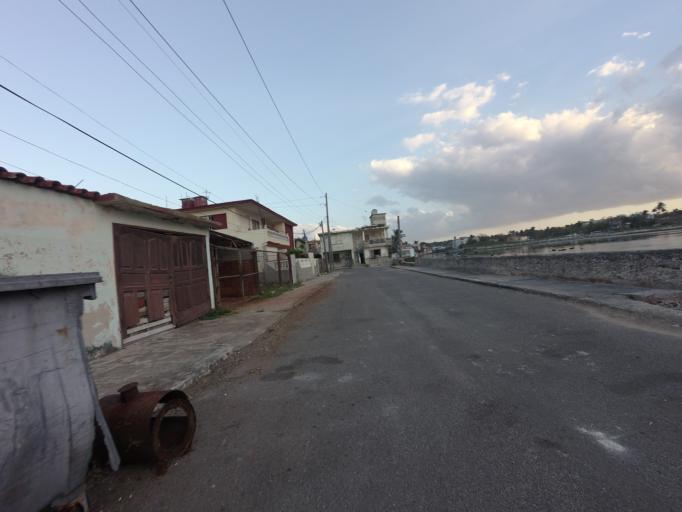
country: CU
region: La Habana
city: Cerro
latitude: 23.0946
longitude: -82.4613
